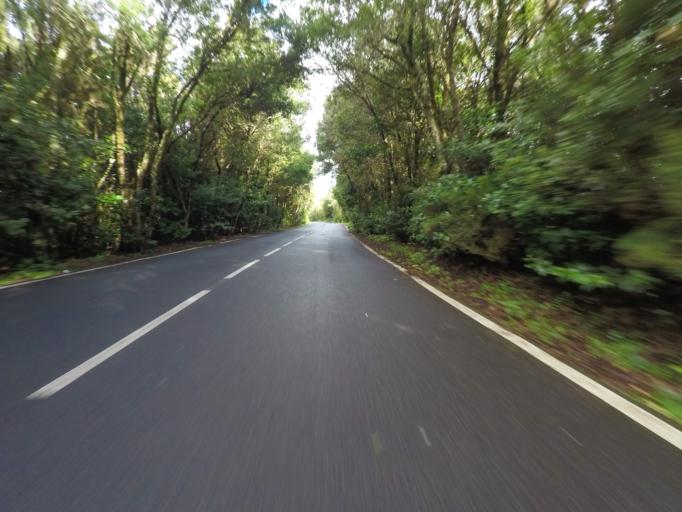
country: ES
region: Canary Islands
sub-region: Provincia de Santa Cruz de Tenerife
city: Hermigua
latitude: 28.1165
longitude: -17.2185
